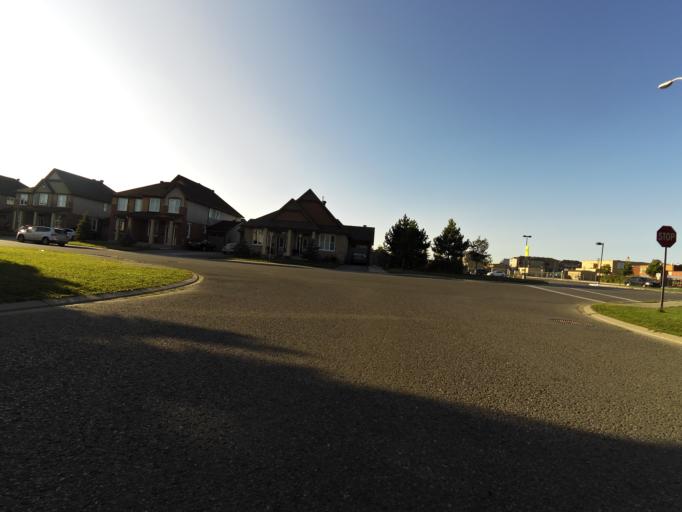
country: CA
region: Ontario
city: Bells Corners
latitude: 45.2869
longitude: -75.7271
